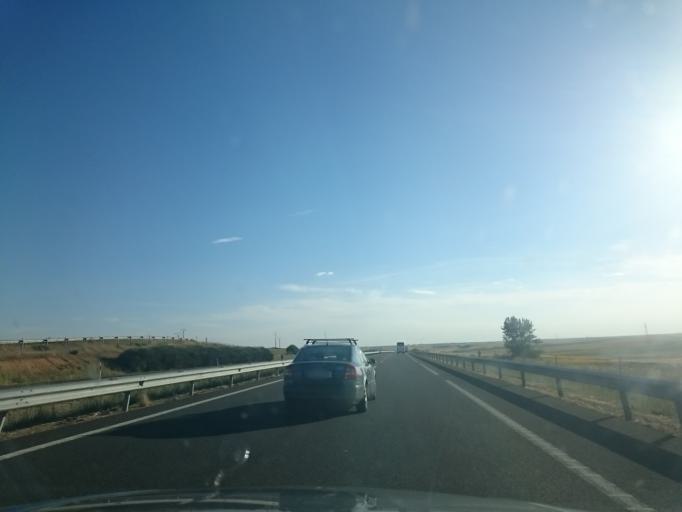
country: ES
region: Castille and Leon
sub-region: Provincia de Palencia
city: Villasarracino
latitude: 42.3780
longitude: -4.5113
